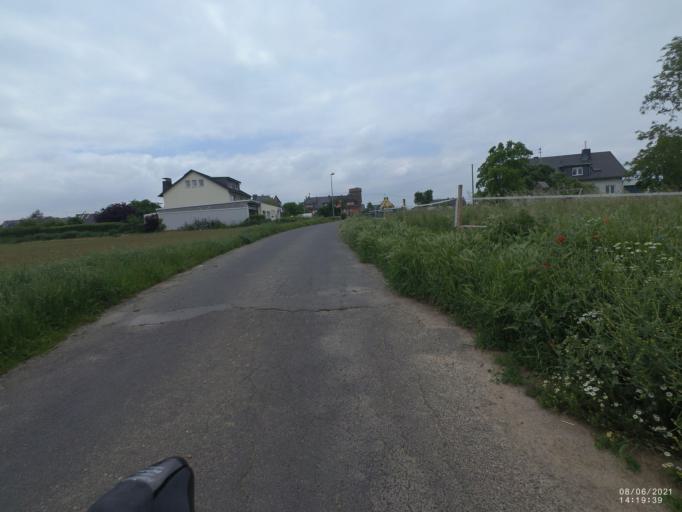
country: DE
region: Rheinland-Pfalz
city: Munstermaifeld
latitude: 50.2471
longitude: 7.3676
